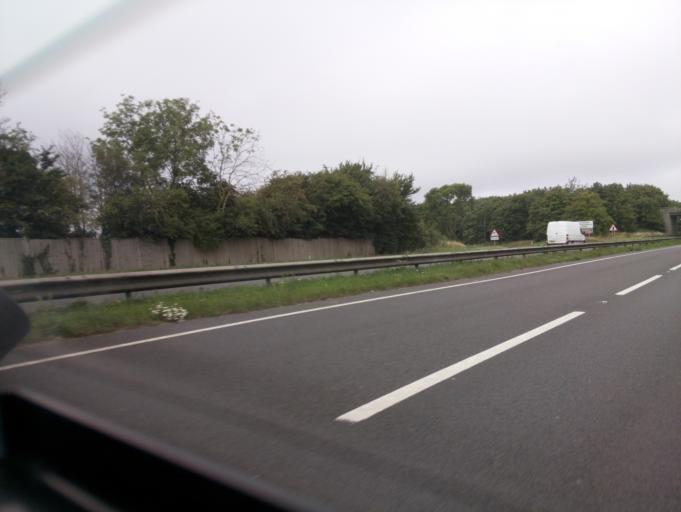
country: GB
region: England
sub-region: Wiltshire
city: Cricklade
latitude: 51.6403
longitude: -1.8421
